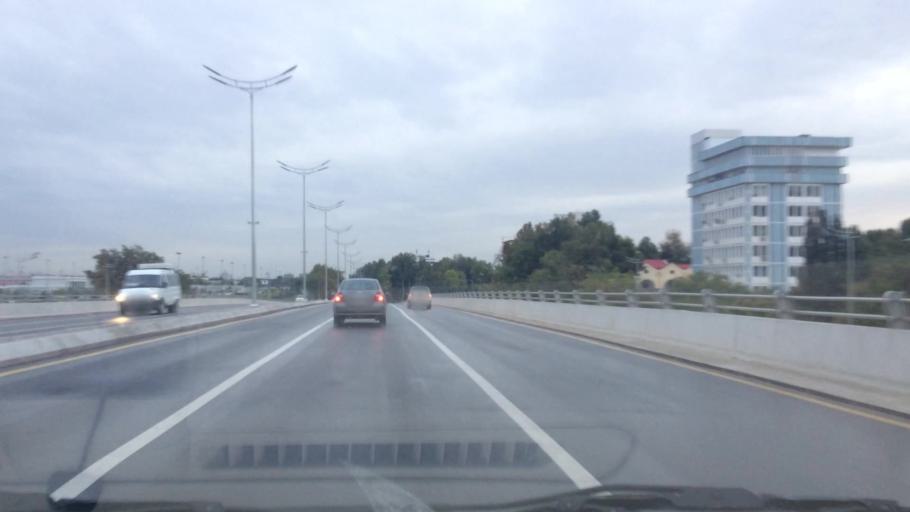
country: UZ
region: Toshkent Shahri
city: Tashkent
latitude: 41.2821
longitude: 69.2118
